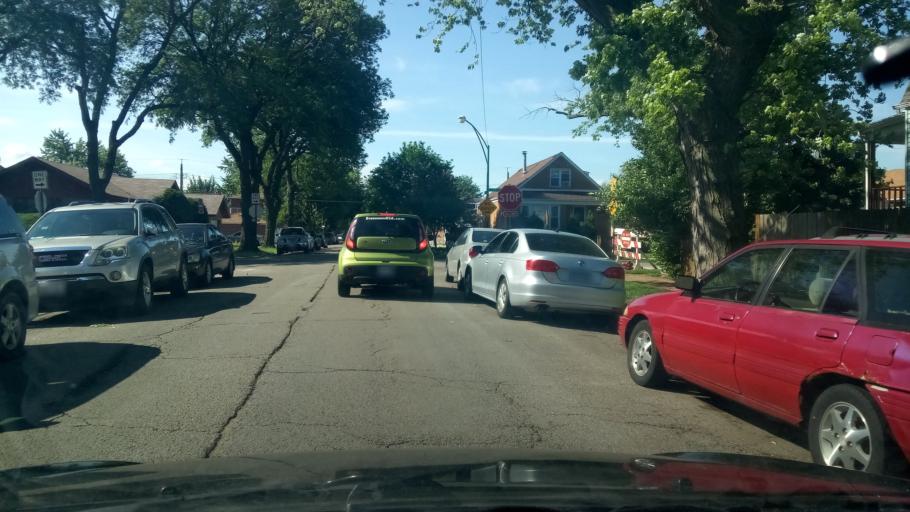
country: US
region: Illinois
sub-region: Cook County
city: Hometown
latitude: 41.7781
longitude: -87.7203
